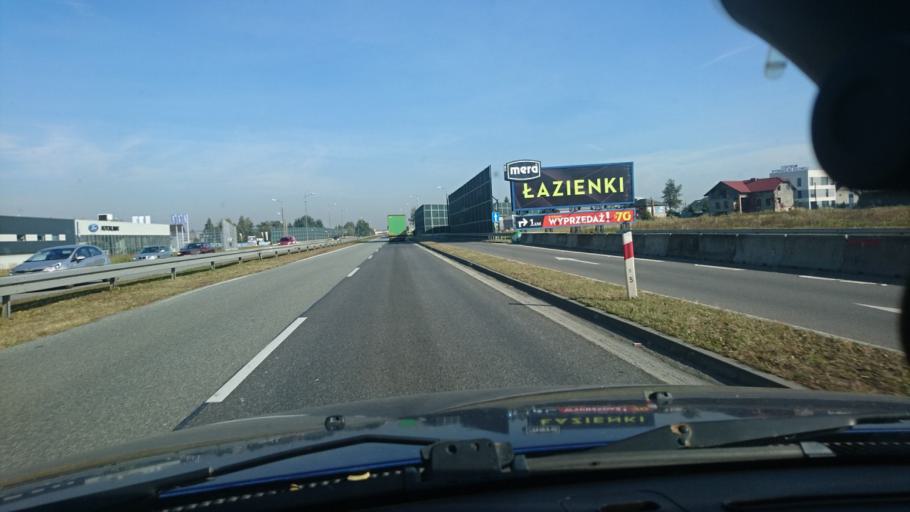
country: PL
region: Silesian Voivodeship
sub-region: Tychy
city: Cielmice
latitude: 50.0844
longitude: 19.0037
